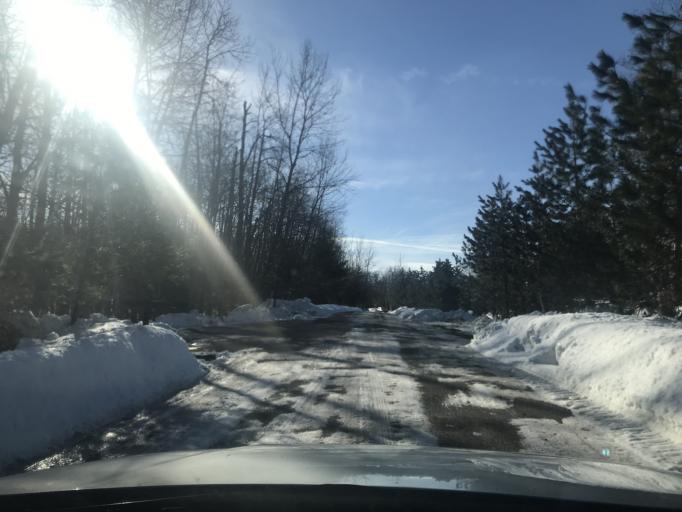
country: US
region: Wisconsin
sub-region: Marinette County
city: Niagara
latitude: 45.4239
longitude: -88.0210
